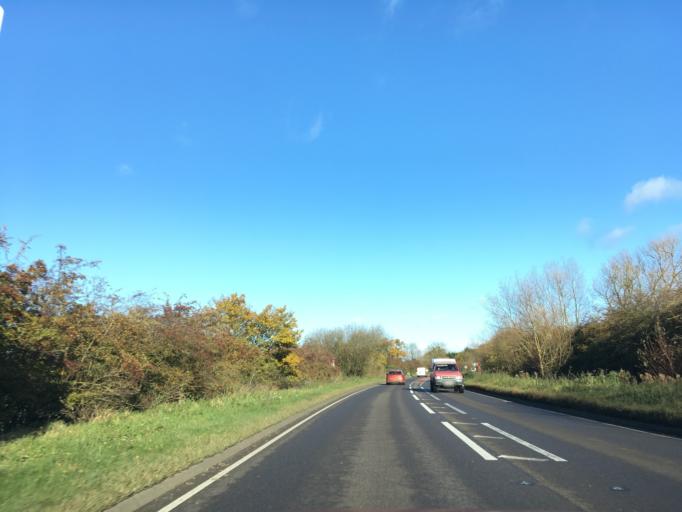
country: GB
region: England
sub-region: Worcestershire
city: Evesham
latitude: 52.0365
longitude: -1.9916
